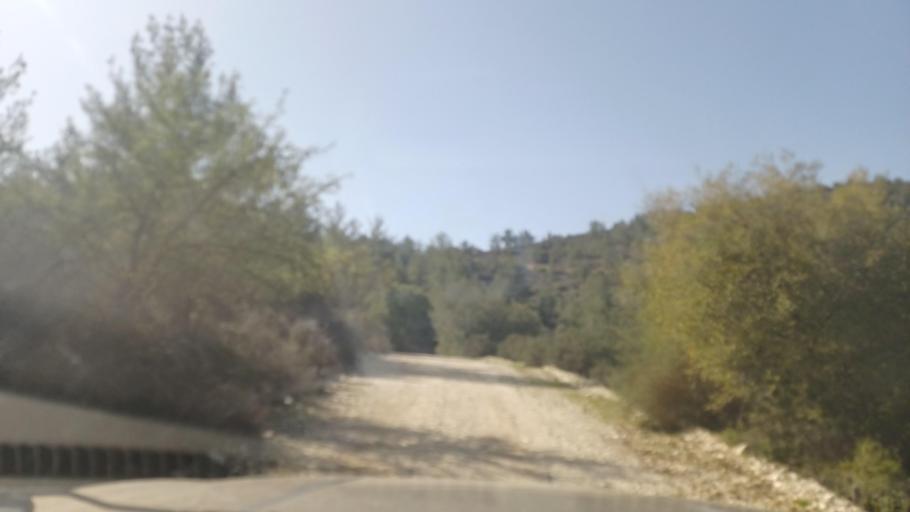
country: CY
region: Limassol
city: Pachna
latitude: 34.8902
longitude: 32.7247
